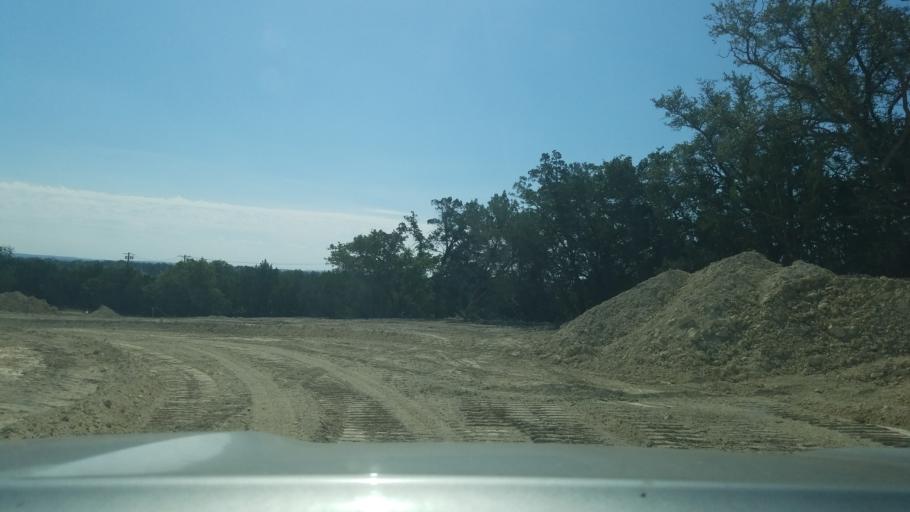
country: US
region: Texas
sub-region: Kendall County
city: Boerne
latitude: 29.7572
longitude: -98.7172
